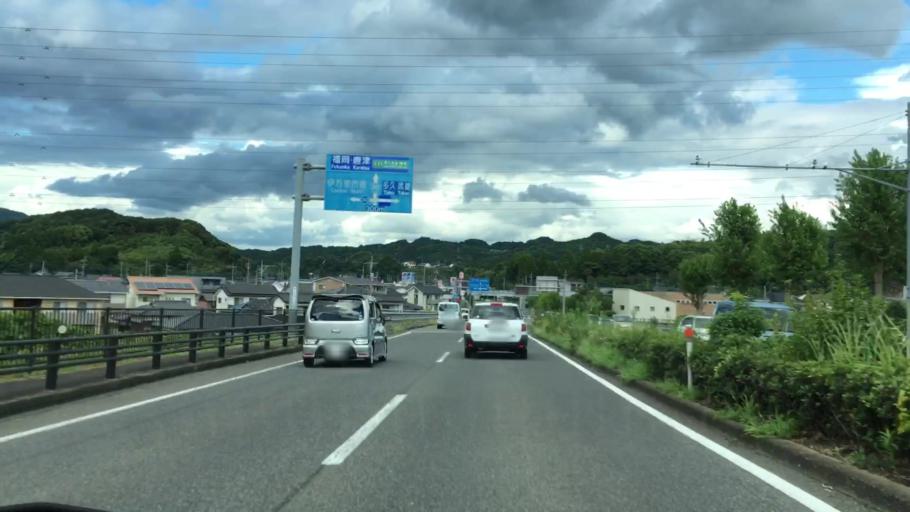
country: JP
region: Saga Prefecture
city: Imaricho-ko
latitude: 33.2712
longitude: 129.8877
